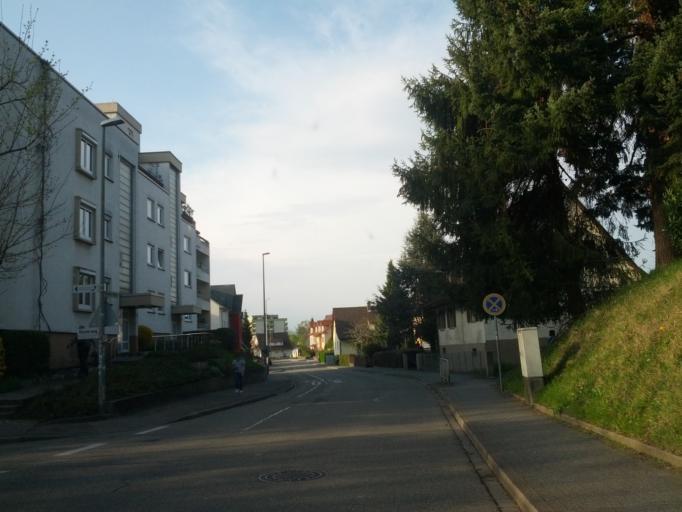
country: DE
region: Baden-Wuerttemberg
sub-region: Freiburg Region
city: Gundelfingen
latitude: 48.0442
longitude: 7.8643
